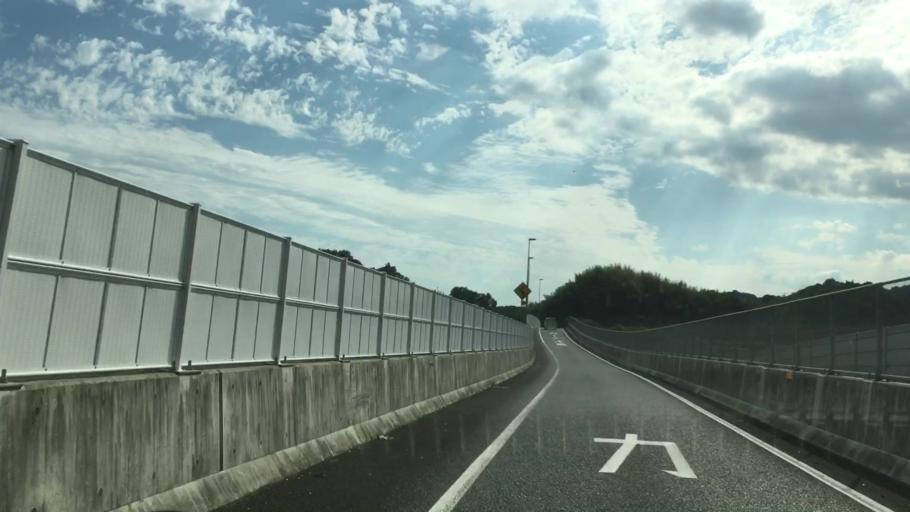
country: JP
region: Hiroshima
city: Hatsukaichi
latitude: 34.3485
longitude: 132.3187
